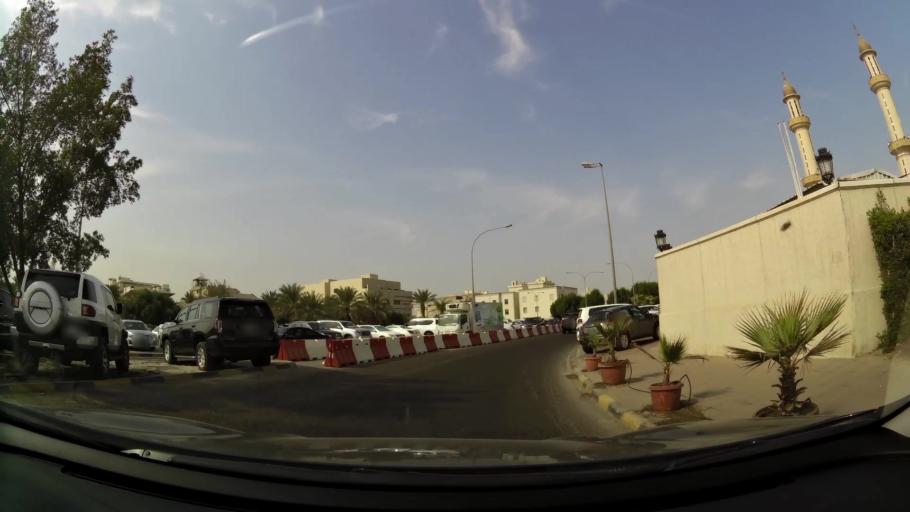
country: KW
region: Al Asimah
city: Ash Shamiyah
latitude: 29.3186
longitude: 47.9696
